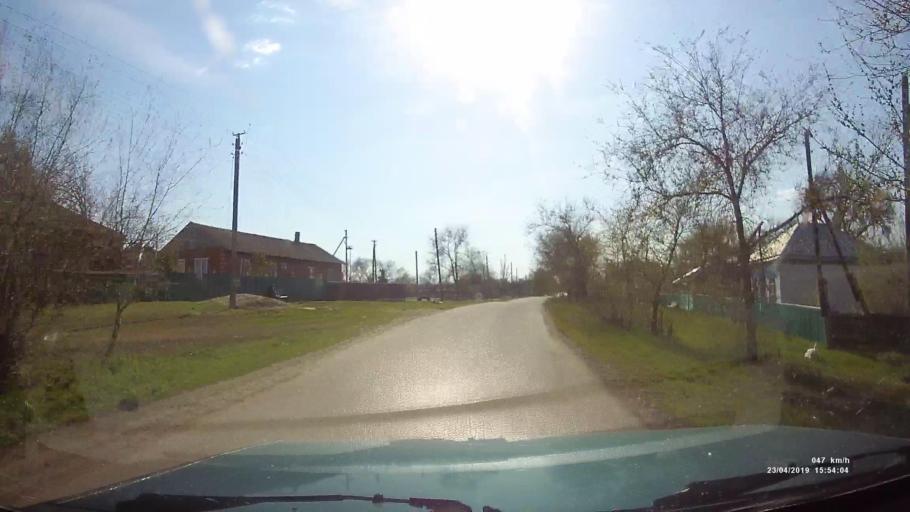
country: RU
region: Rostov
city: Remontnoye
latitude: 46.5370
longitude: 43.1310
